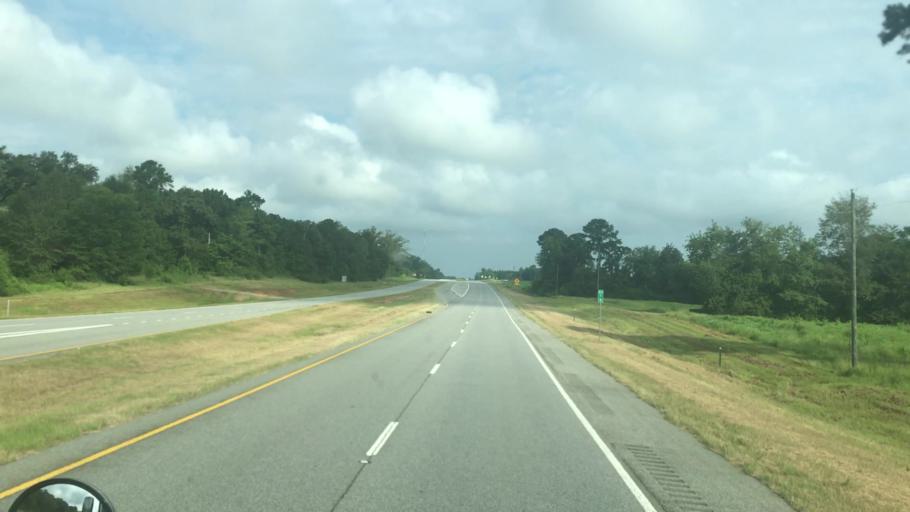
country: US
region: Georgia
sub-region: Miller County
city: Colquitt
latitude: 31.2515
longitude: -84.7995
